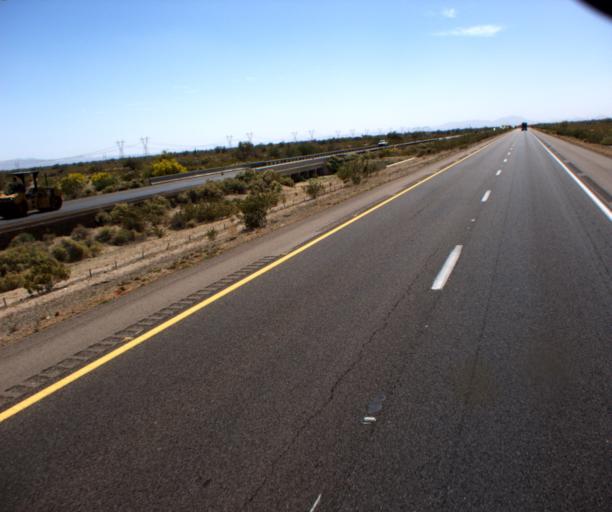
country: US
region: Arizona
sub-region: Maricopa County
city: Gila Bend
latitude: 33.0073
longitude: -112.6561
